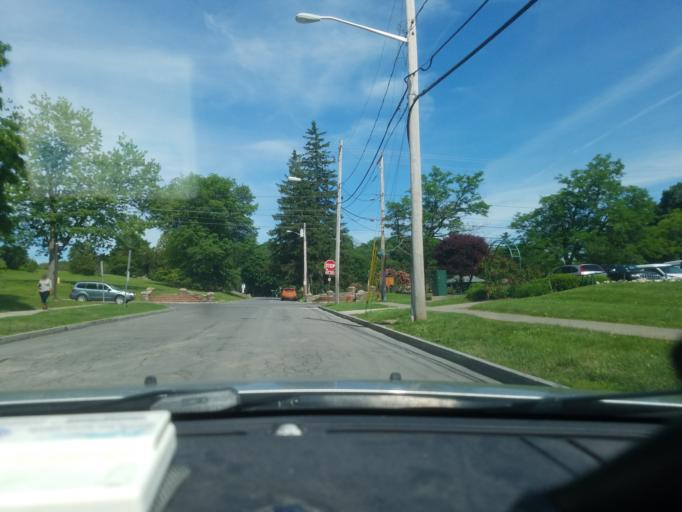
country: US
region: New York
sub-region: Onondaga County
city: Syracuse
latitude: 43.0394
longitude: -76.1290
